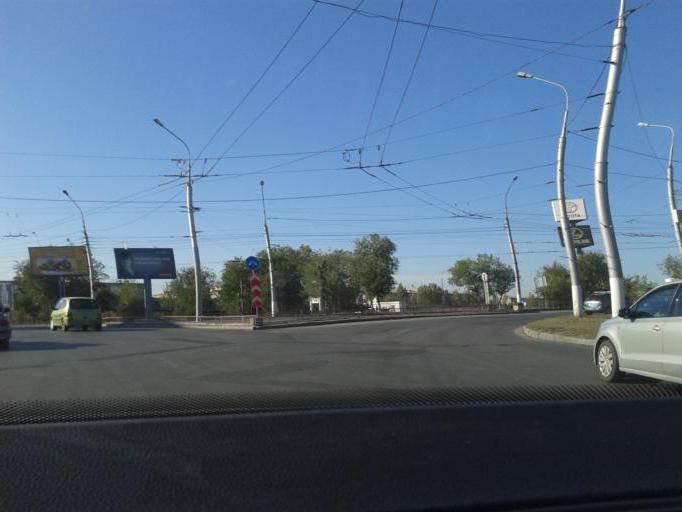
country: RU
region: Volgograd
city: Volgograd
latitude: 48.7551
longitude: 44.4806
